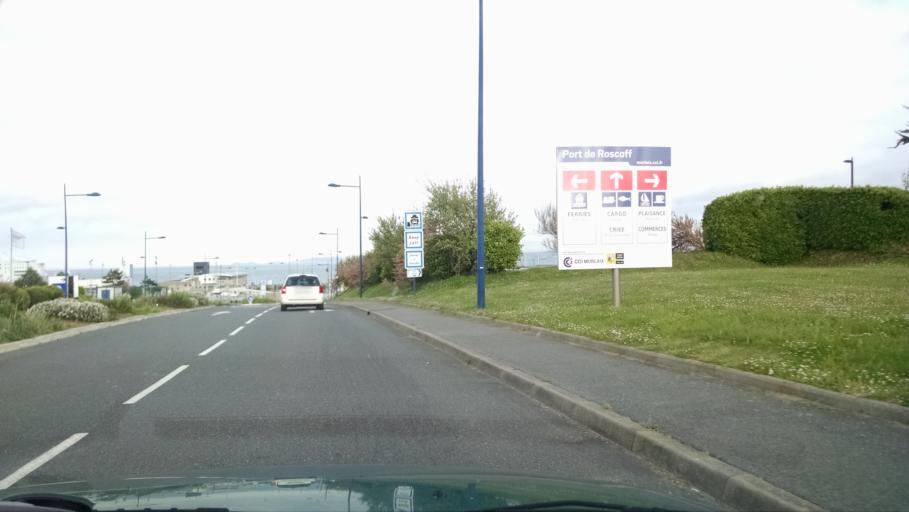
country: FR
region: Brittany
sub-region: Departement du Finistere
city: Roscoff
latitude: 48.7189
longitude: -3.9719
